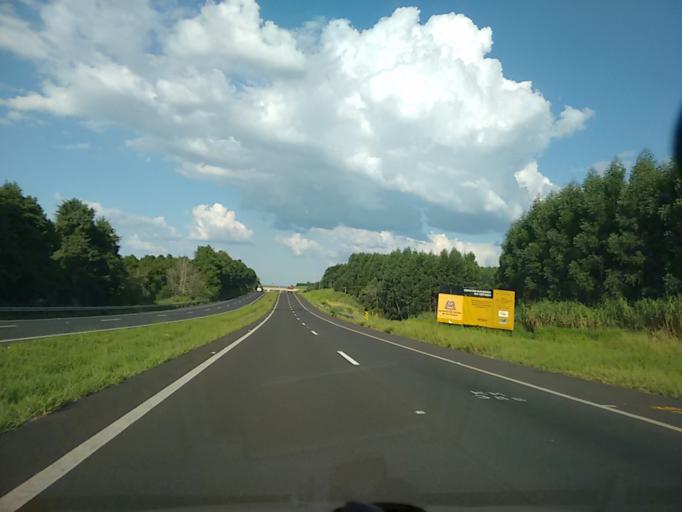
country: BR
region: Sao Paulo
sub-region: Duartina
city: Duartina
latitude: -22.3283
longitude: -49.4428
